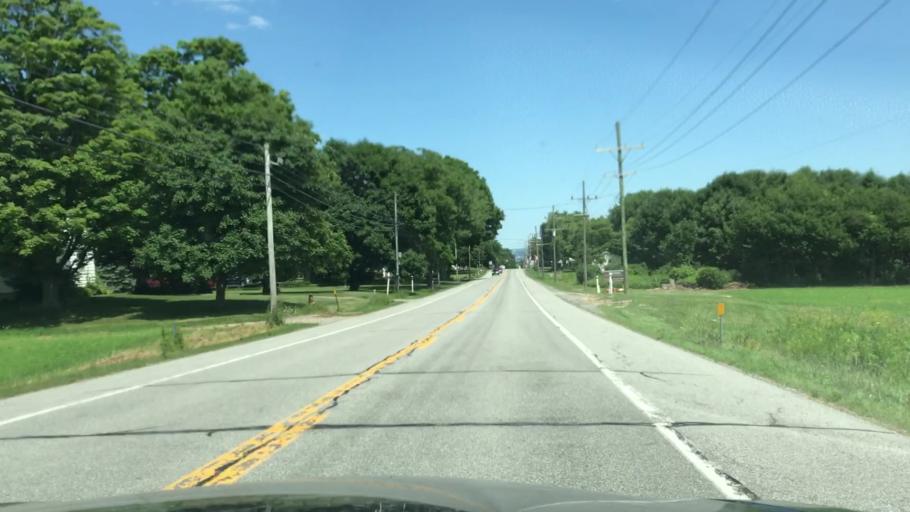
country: US
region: New York
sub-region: Wyoming County
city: Perry
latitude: 42.7484
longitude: -78.0112
